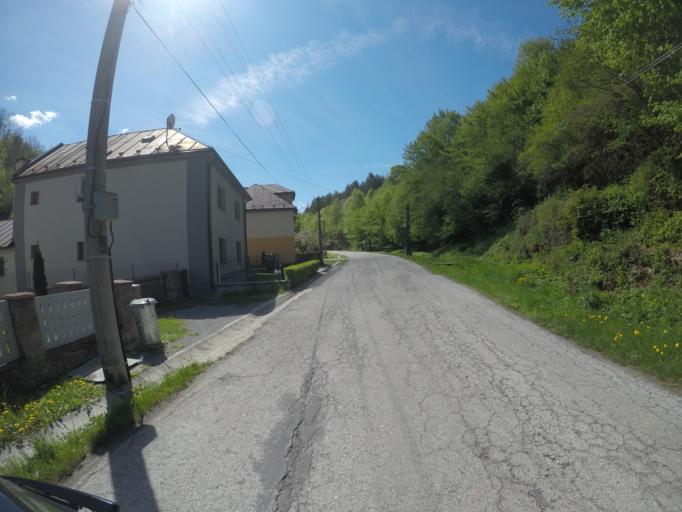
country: SK
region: Banskobystricky
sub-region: Okres Banska Bystrica
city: Banska Bystrica
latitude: 48.7182
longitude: 19.2267
